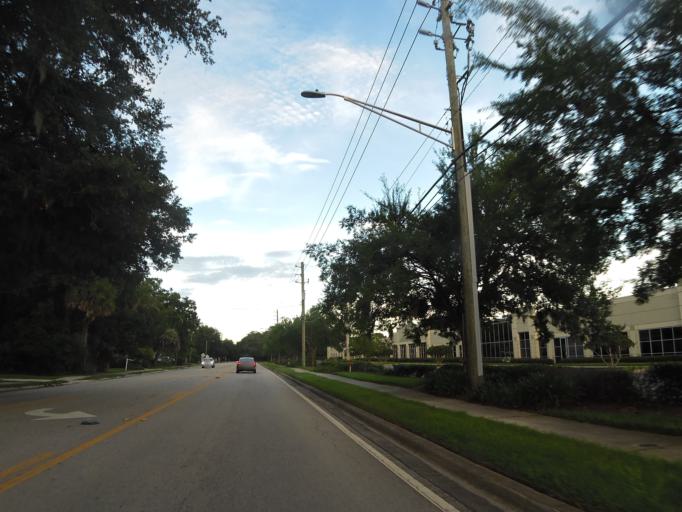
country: US
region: Florida
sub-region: Duval County
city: Jacksonville
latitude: 30.2643
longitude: -81.5957
